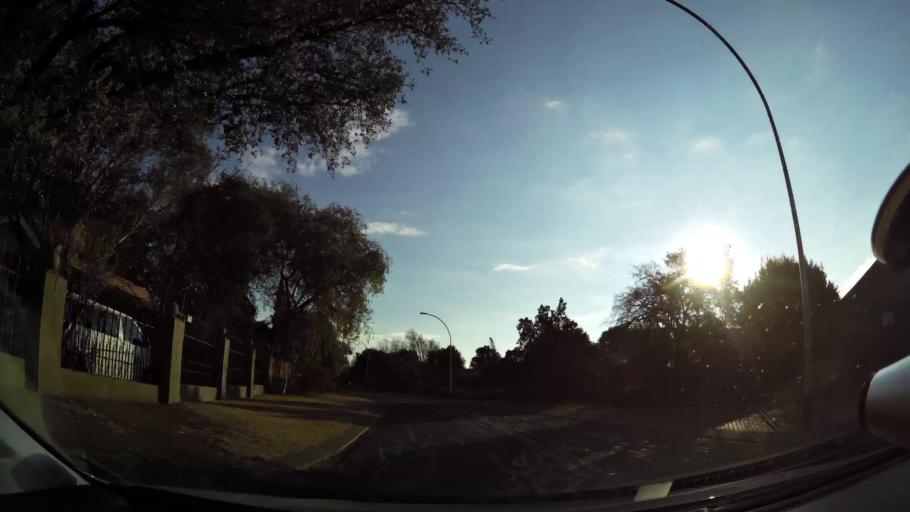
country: ZA
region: Orange Free State
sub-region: Mangaung Metropolitan Municipality
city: Bloemfontein
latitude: -29.1536
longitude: 26.1801
